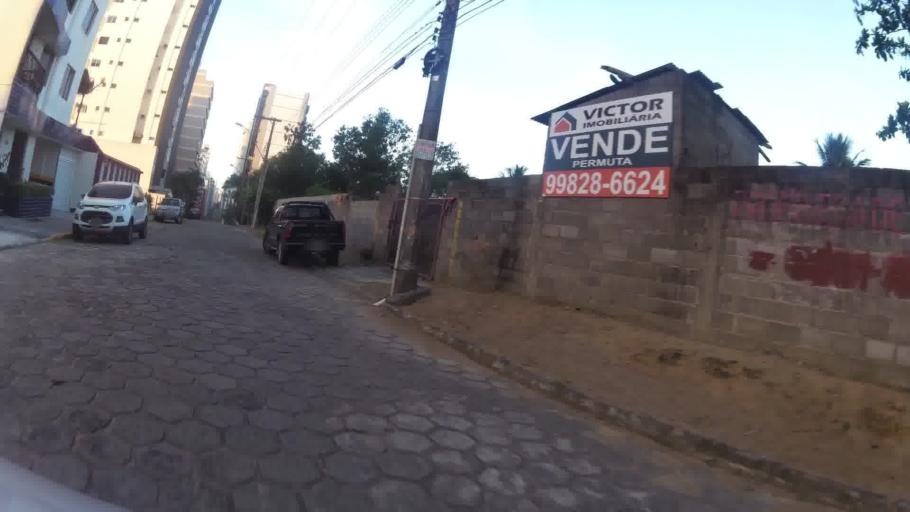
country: BR
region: Espirito Santo
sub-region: Guarapari
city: Guarapari
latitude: -20.6768
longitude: -40.5029
